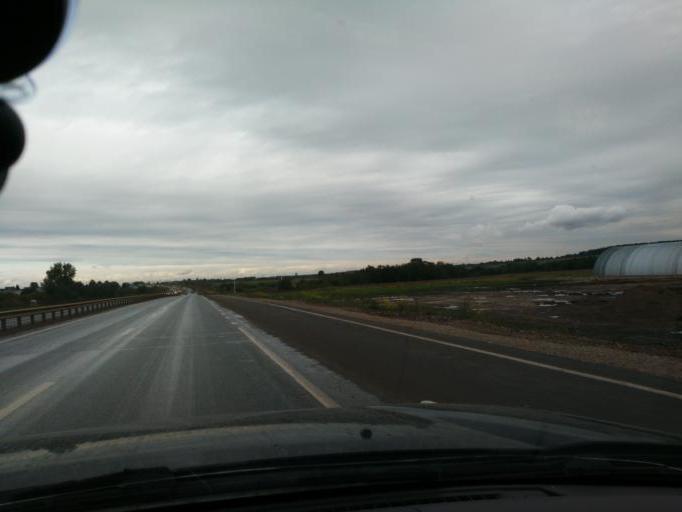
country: RU
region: Perm
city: Kultayevo
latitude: 57.9023
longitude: 55.9781
